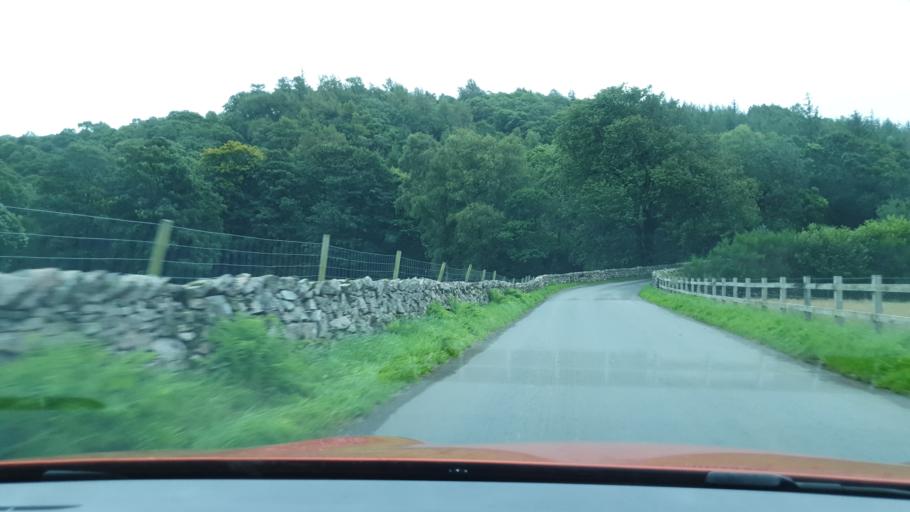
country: GB
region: England
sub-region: Cumbria
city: Seascale
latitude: 54.3848
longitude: -3.3118
